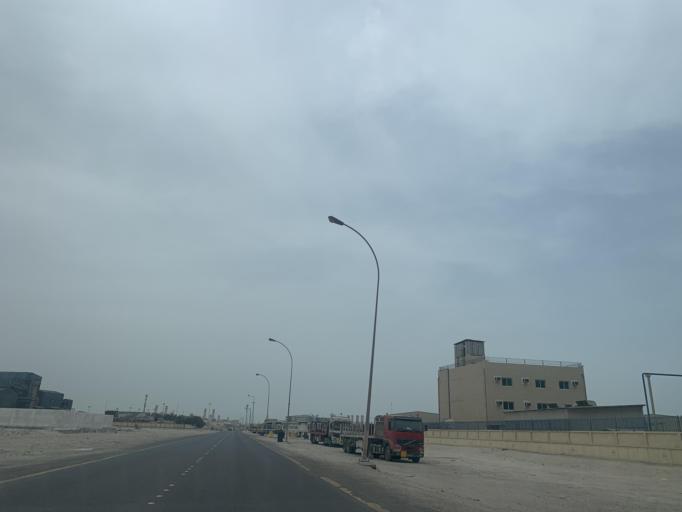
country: BH
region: Muharraq
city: Al Hadd
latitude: 26.2069
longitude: 50.6746
